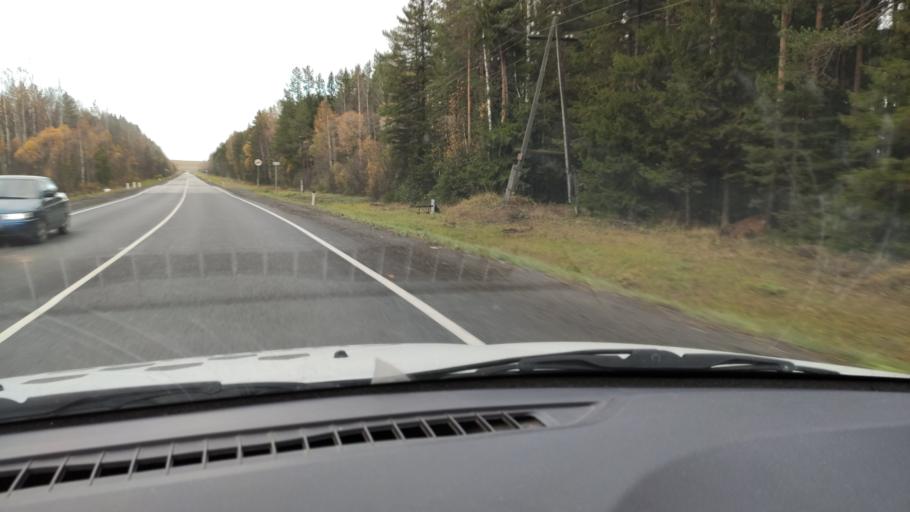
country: RU
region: Kirov
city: Belaya Kholunitsa
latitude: 58.8801
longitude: 50.8715
